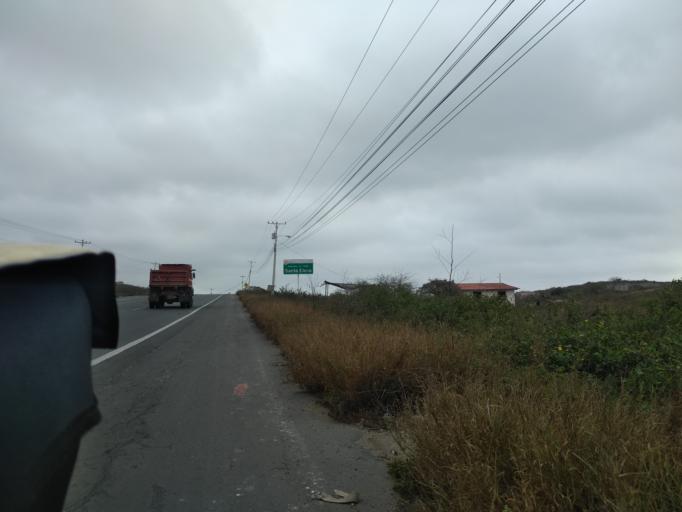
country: EC
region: Santa Elena
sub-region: Canton Santa Elena
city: Santa Elena
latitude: -2.2060
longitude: -80.8605
